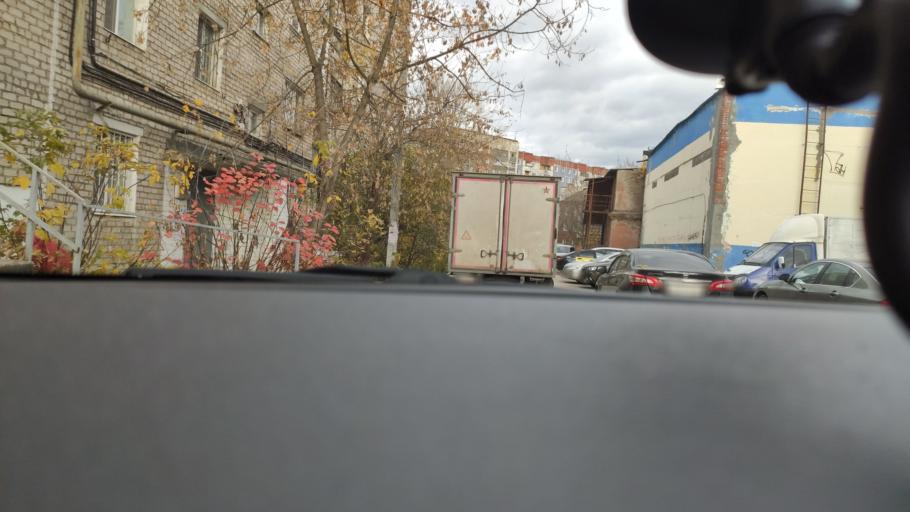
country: RU
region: Perm
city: Perm
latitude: 57.9688
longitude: 56.2694
